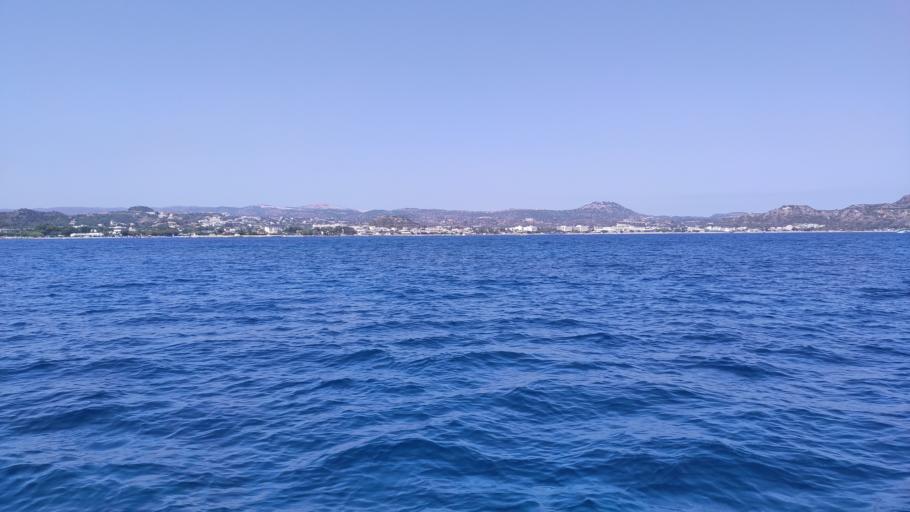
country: GR
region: South Aegean
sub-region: Nomos Dodekanisou
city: Faliraki
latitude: 36.3341
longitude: 28.2192
